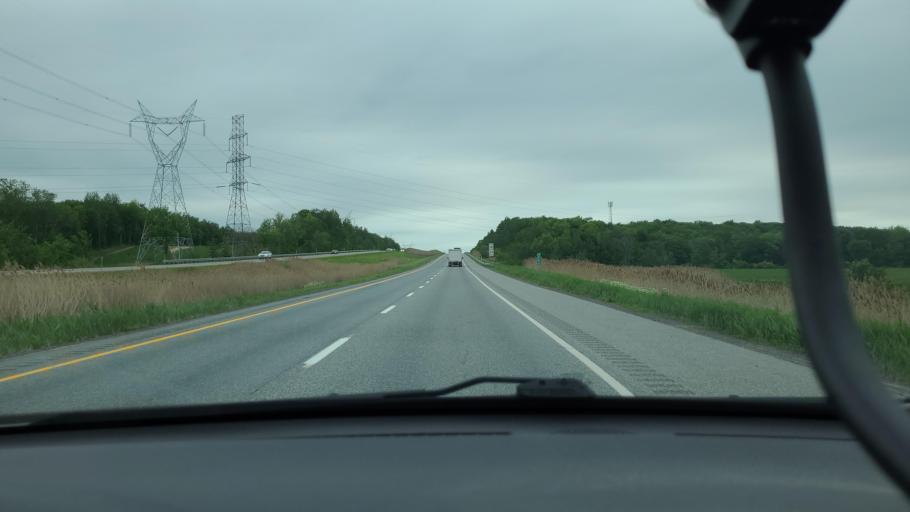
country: CA
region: Quebec
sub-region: Lanaudiere
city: Mascouche
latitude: 45.7952
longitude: -73.5830
